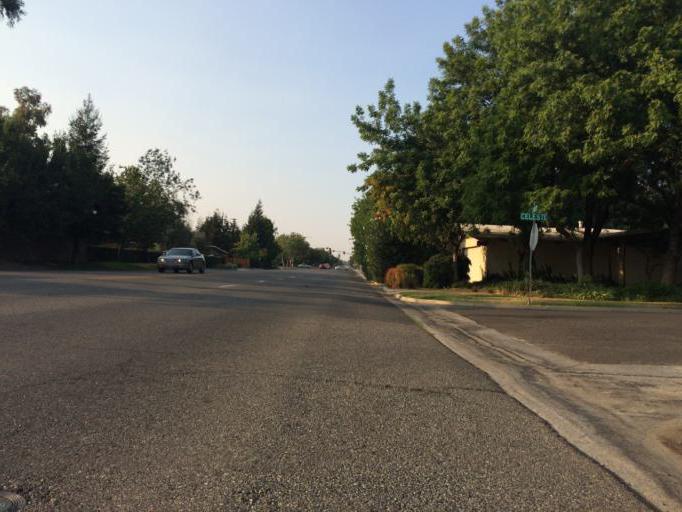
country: US
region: California
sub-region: Fresno County
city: Fresno
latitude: 36.8209
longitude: -119.8173
